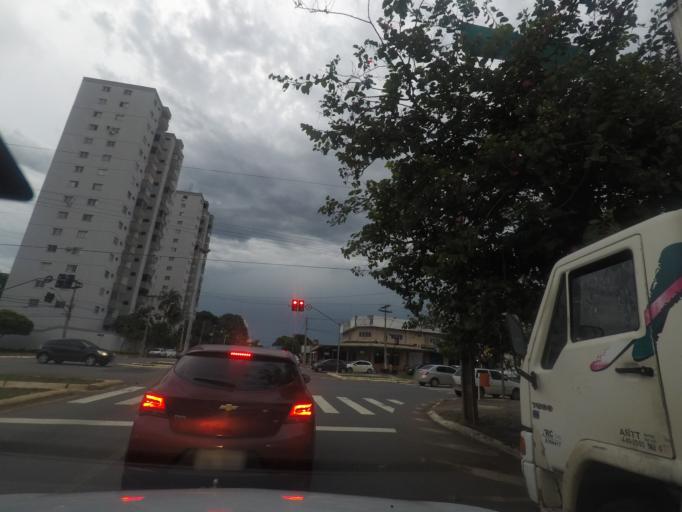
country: BR
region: Goias
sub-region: Goiania
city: Goiania
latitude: -16.7134
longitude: -49.2505
